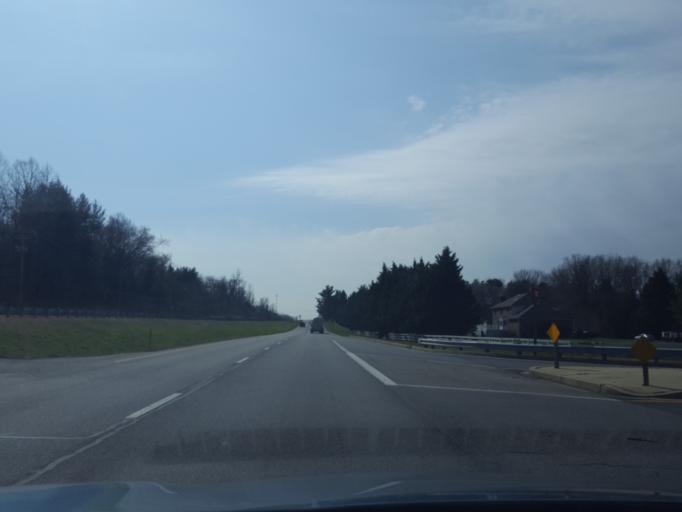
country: US
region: Maryland
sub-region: Calvert County
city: Dunkirk
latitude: 38.7464
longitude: -76.6623
